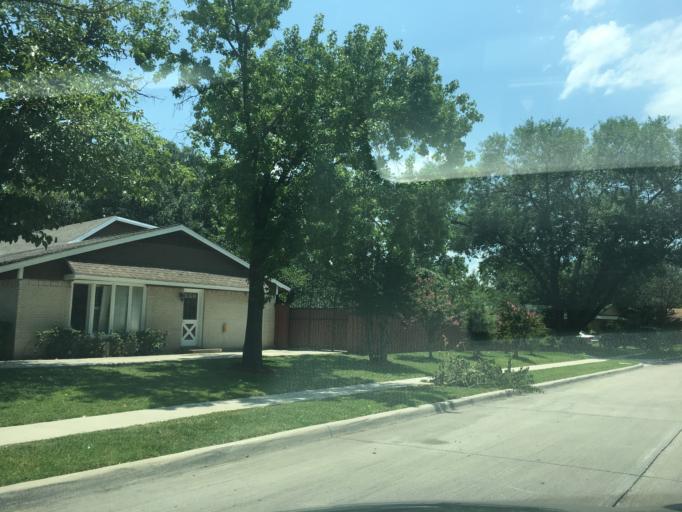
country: US
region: Texas
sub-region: Dallas County
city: Carrollton
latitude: 32.9503
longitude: -96.8766
